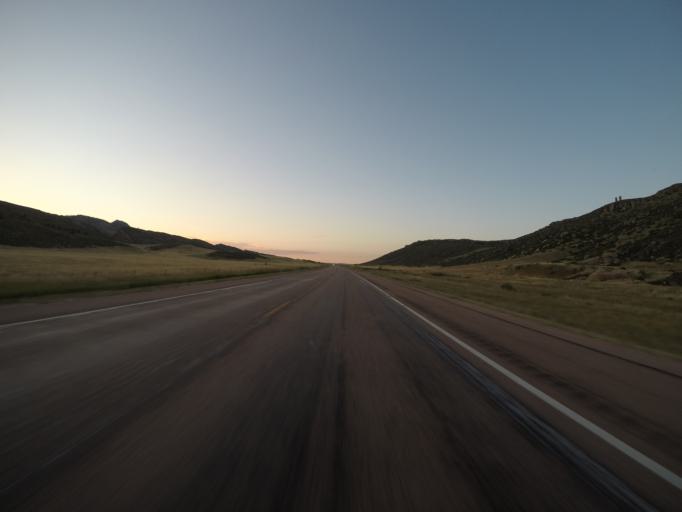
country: US
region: Colorado
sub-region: Larimer County
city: Laporte
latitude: 40.7071
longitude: -105.1732
